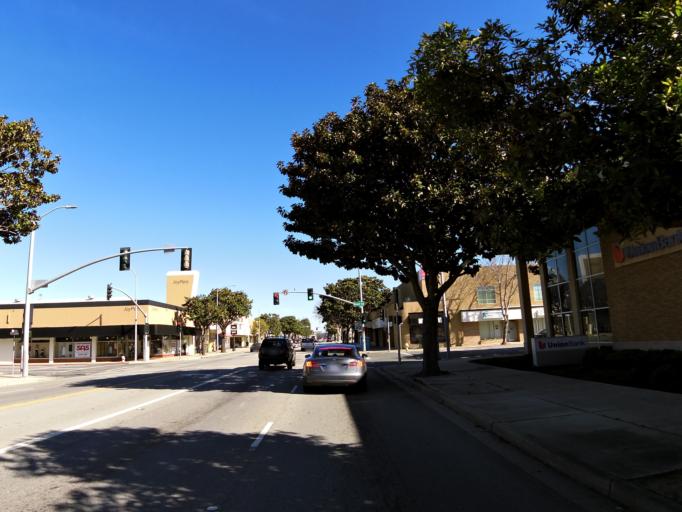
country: US
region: California
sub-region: Monterey County
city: Salinas
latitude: 36.6623
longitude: -121.6579
